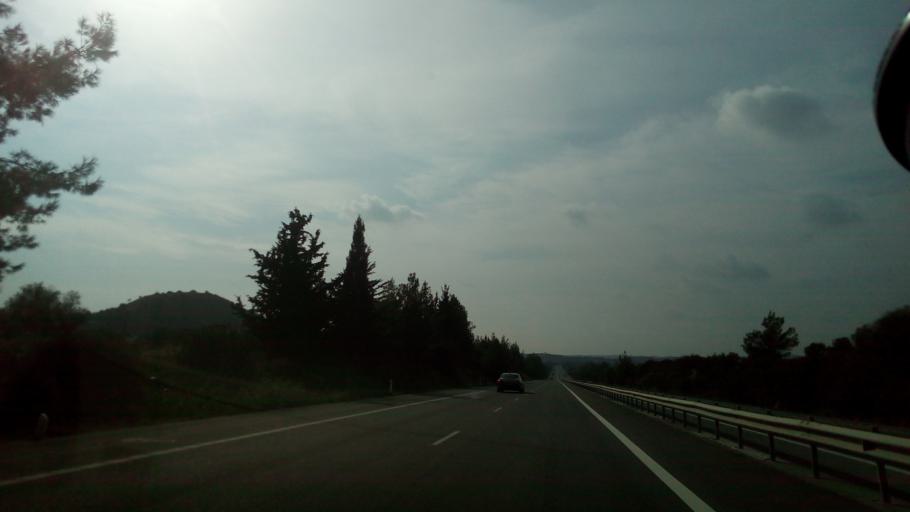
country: CY
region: Larnaka
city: Kofinou
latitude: 34.8398
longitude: 33.4235
